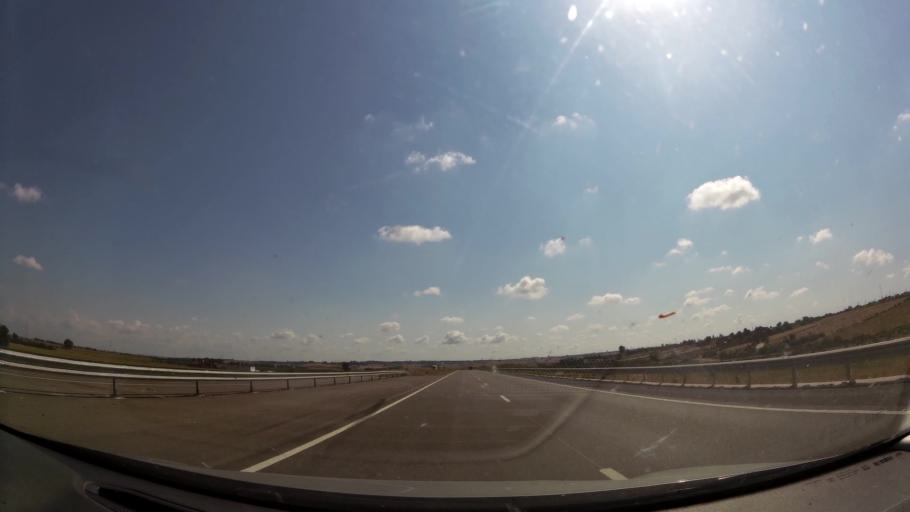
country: MA
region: Rabat-Sale-Zemmour-Zaer
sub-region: Skhirate-Temara
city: Temara
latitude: 33.8688
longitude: -6.8048
